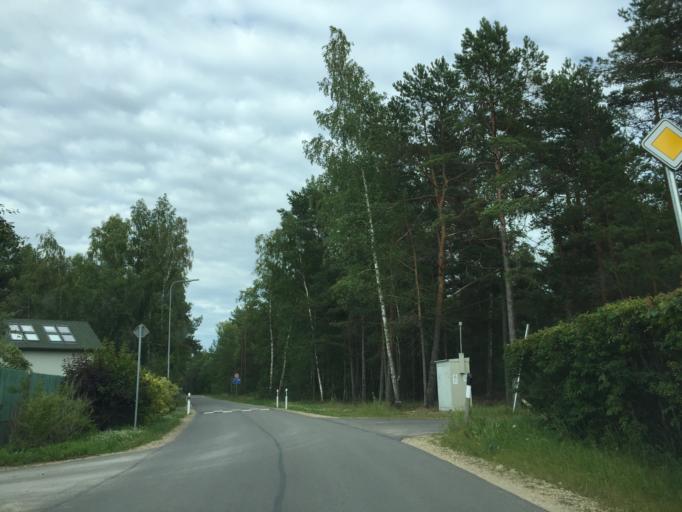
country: LV
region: Carnikava
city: Carnikava
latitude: 57.1319
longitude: 24.2549
